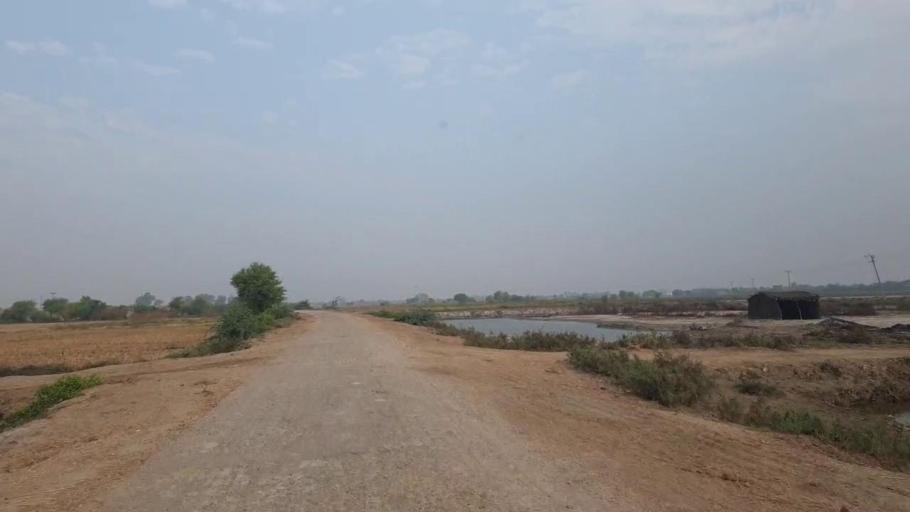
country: PK
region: Sindh
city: Tando Bago
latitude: 24.7855
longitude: 68.8869
